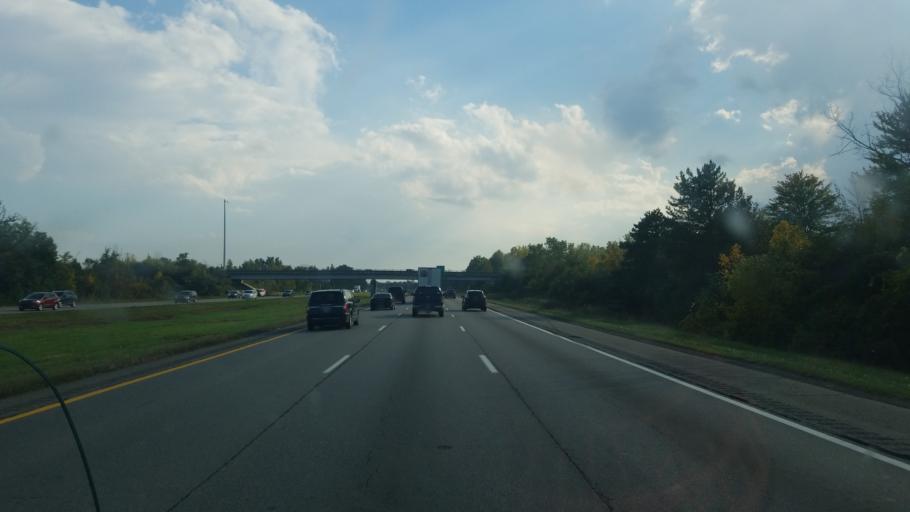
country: US
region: Michigan
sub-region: Wayne County
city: Canton
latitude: 42.2963
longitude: -83.4435
